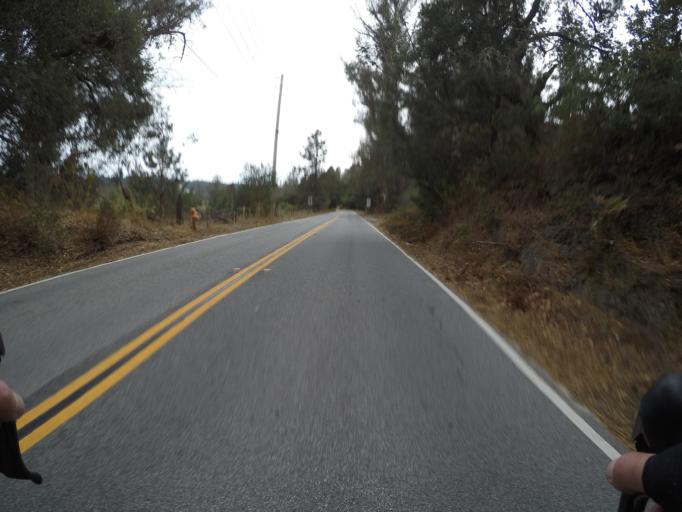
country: US
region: California
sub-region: Santa Cruz County
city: Ben Lomond
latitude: 37.0842
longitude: -122.0645
